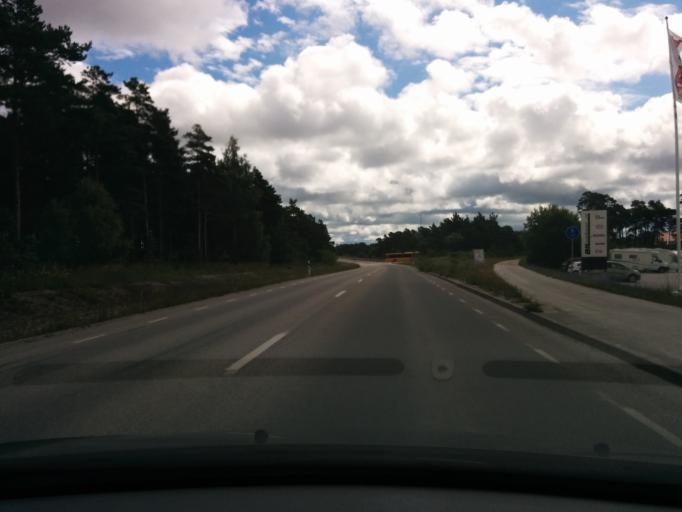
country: SE
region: Gotland
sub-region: Gotland
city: Visby
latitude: 57.6306
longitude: 18.3409
